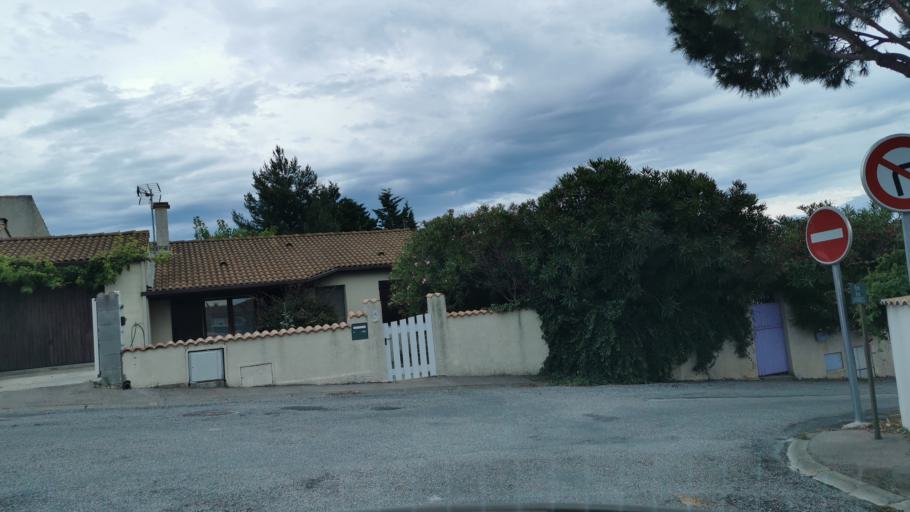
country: FR
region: Languedoc-Roussillon
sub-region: Departement de l'Aude
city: Marcorignan
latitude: 43.2238
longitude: 2.9265
